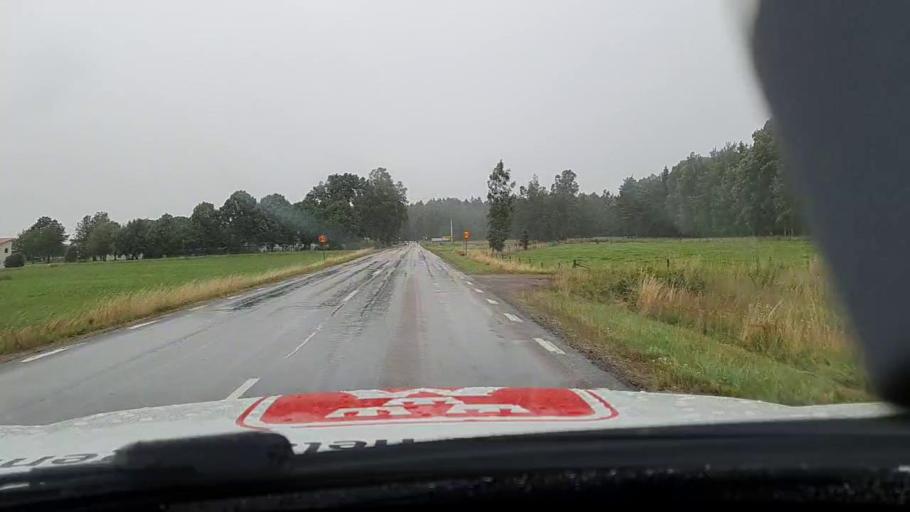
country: SE
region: Vaestra Goetaland
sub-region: Toreboda Kommun
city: Toereboda
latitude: 58.6792
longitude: 14.1325
